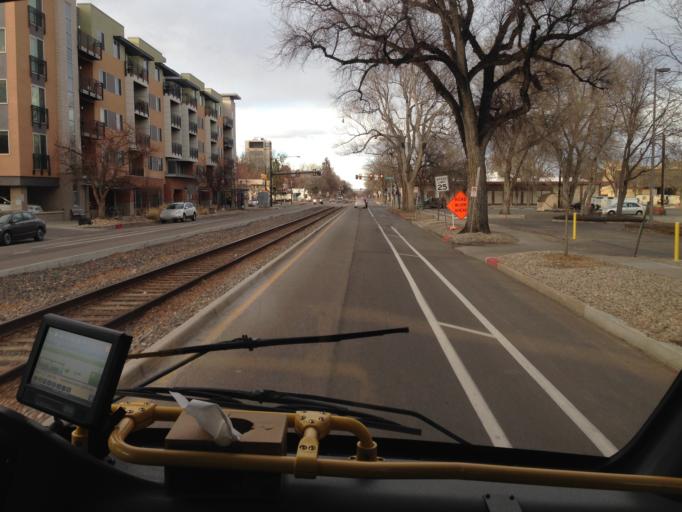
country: US
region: Colorado
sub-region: Larimer County
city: Fort Collins
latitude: 40.5801
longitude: -105.0788
